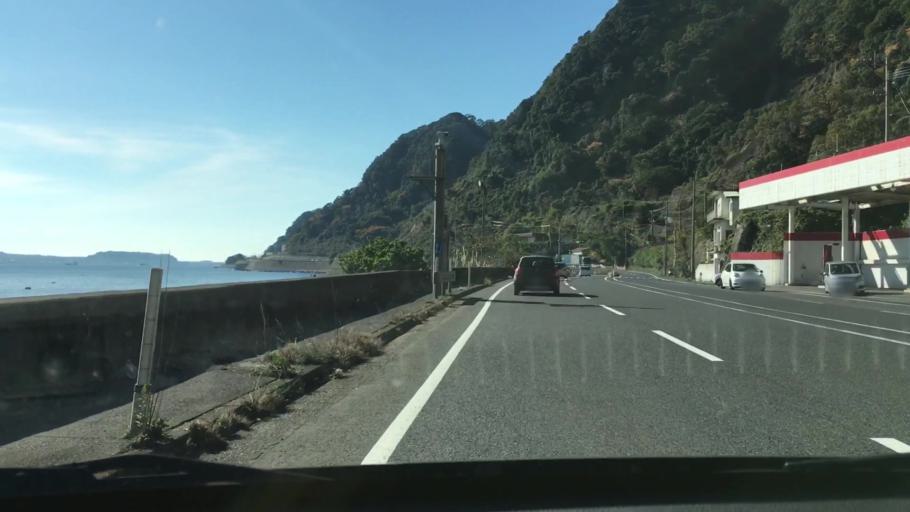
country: JP
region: Kagoshima
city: Kagoshima-shi
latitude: 31.6468
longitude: 130.6043
